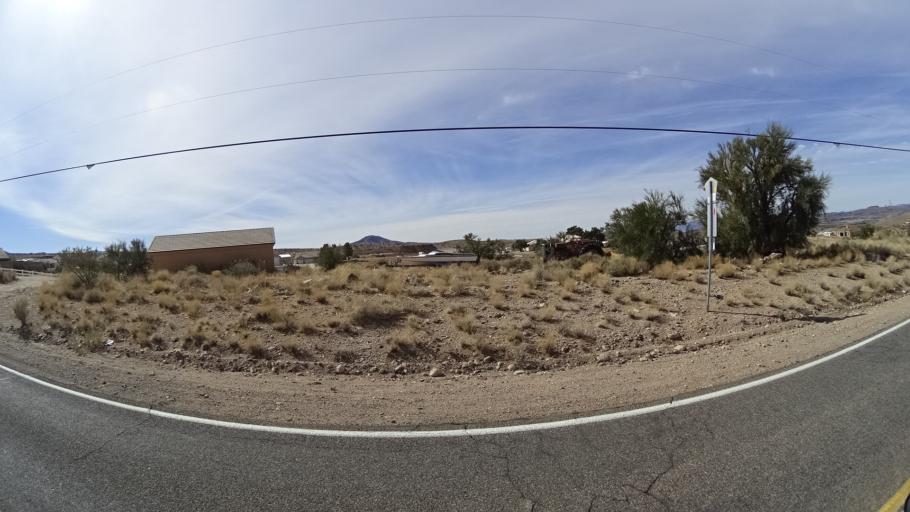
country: US
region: Arizona
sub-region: Mohave County
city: Kingman
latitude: 35.1725
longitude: -113.9832
